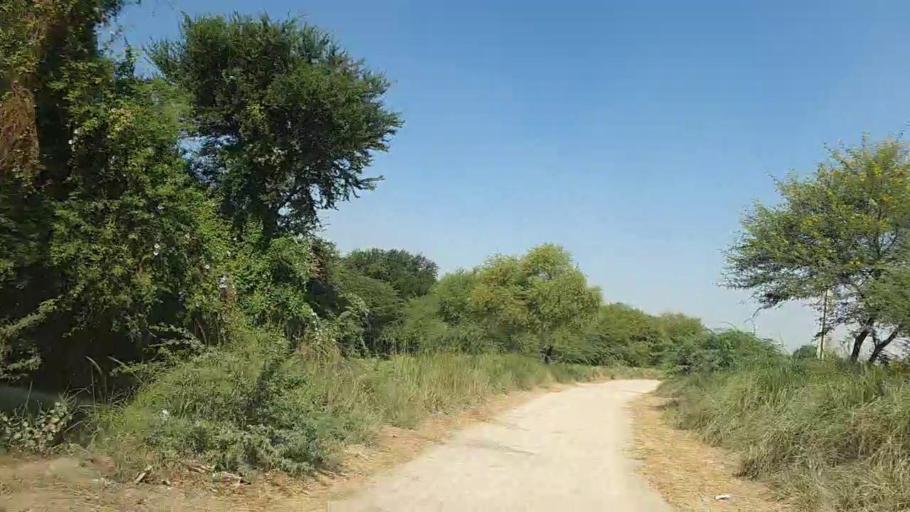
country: PK
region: Sindh
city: Daro Mehar
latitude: 24.7801
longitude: 68.1597
